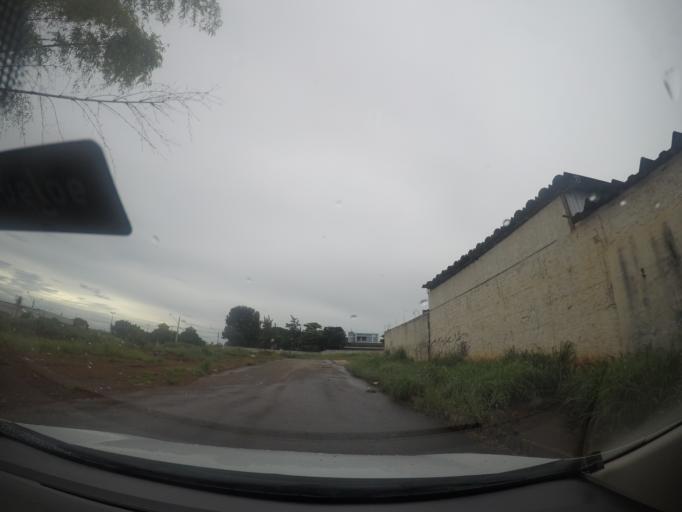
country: BR
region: Goias
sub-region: Goiania
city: Goiania
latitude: -16.6345
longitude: -49.2352
